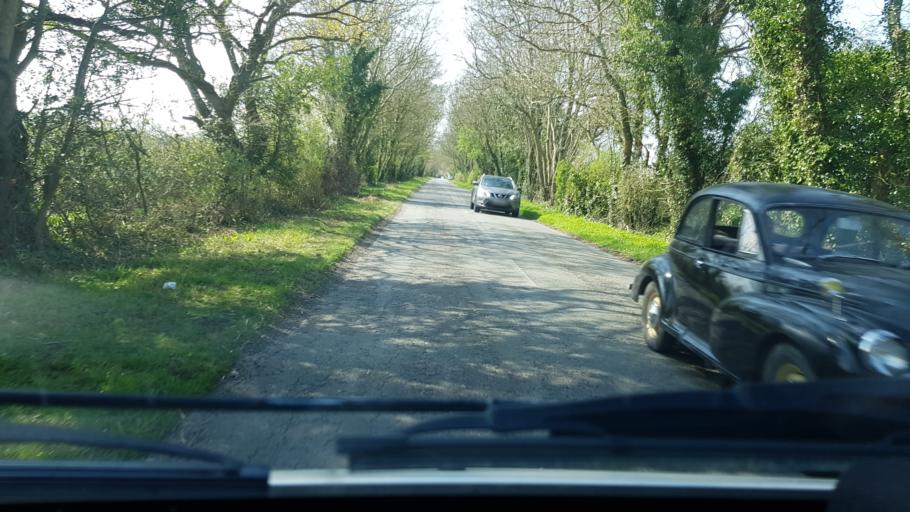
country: GB
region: England
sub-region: West Sussex
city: Chichester
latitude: 50.8615
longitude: -0.7907
